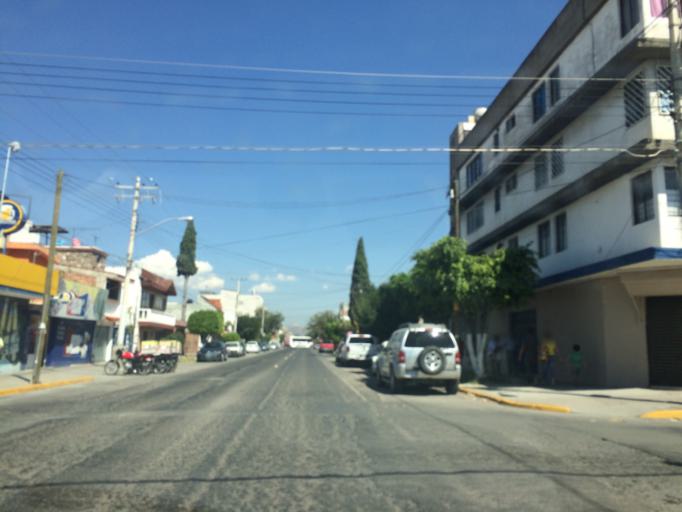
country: MX
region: Guanajuato
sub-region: Leon
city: San Jose de Duran (Los Troncoso)
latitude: 21.0915
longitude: -101.6518
